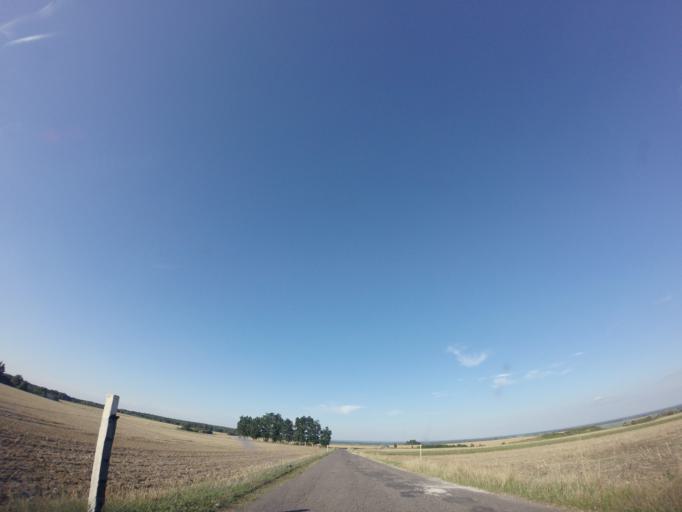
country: PL
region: Lubusz
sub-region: Powiat gorzowski
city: Santok
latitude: 52.7518
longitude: 15.4119
